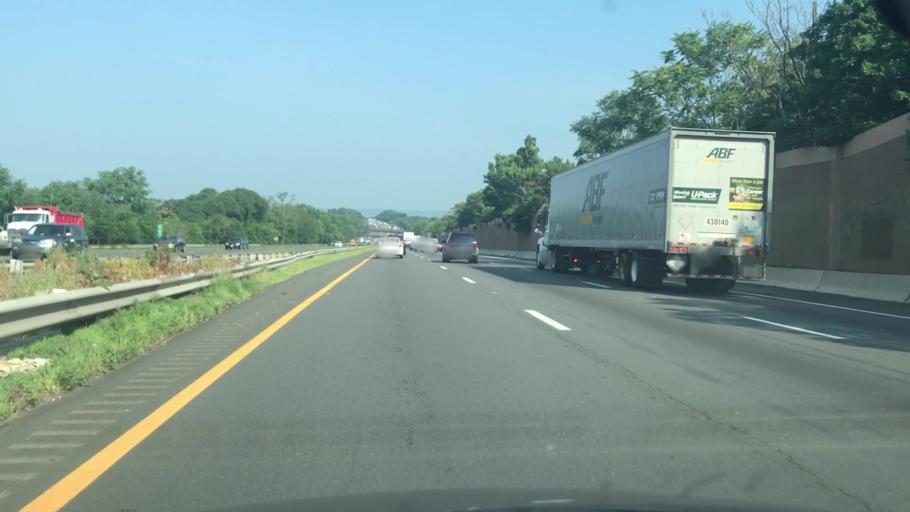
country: US
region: New Jersey
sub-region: Middlesex County
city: Metuchen
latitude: 40.5362
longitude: -74.3810
